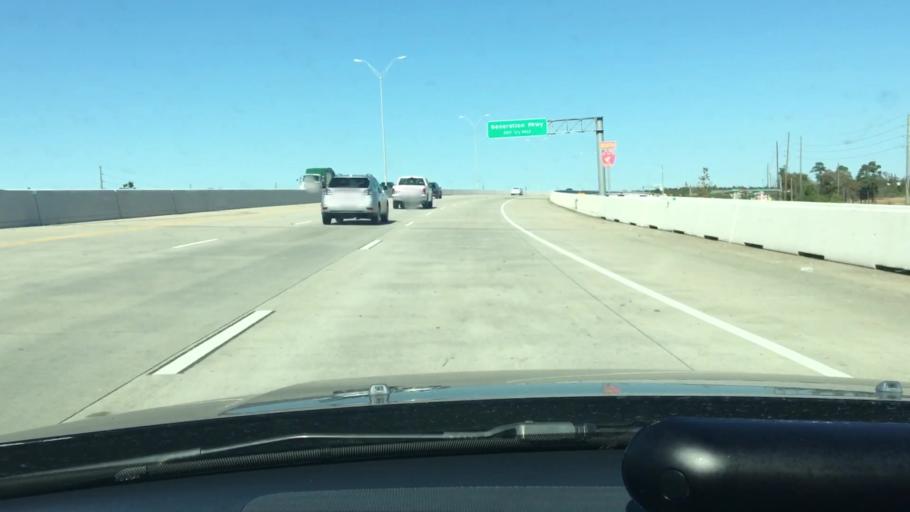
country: US
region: Texas
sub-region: Harris County
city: Sheldon
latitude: 29.8892
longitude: -95.2023
